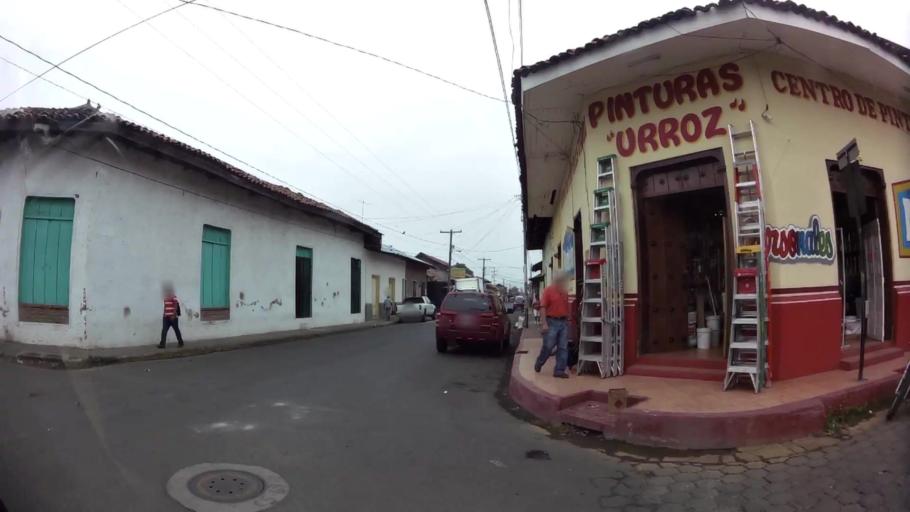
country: NI
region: Leon
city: Leon
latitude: 12.4409
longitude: -86.8760
